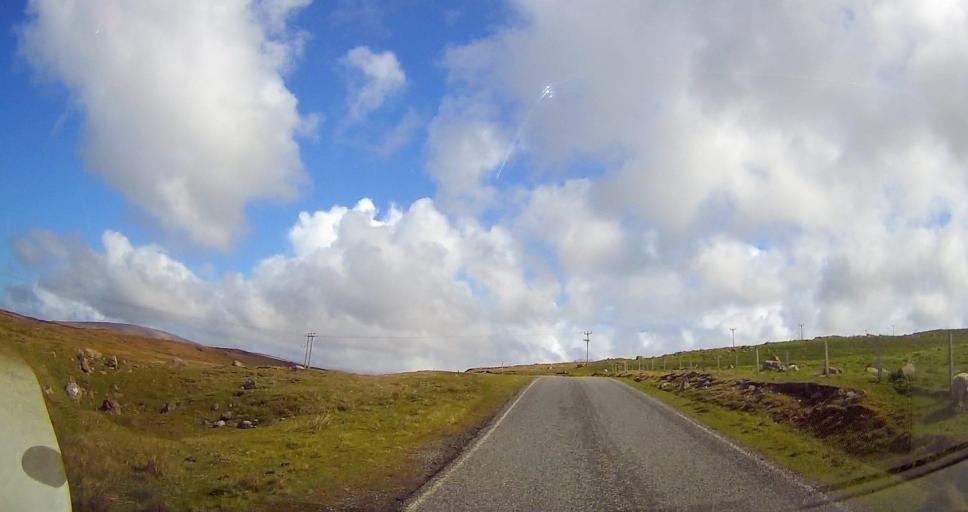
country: GB
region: Scotland
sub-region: Shetland Islands
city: Lerwick
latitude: 60.4803
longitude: -1.4057
